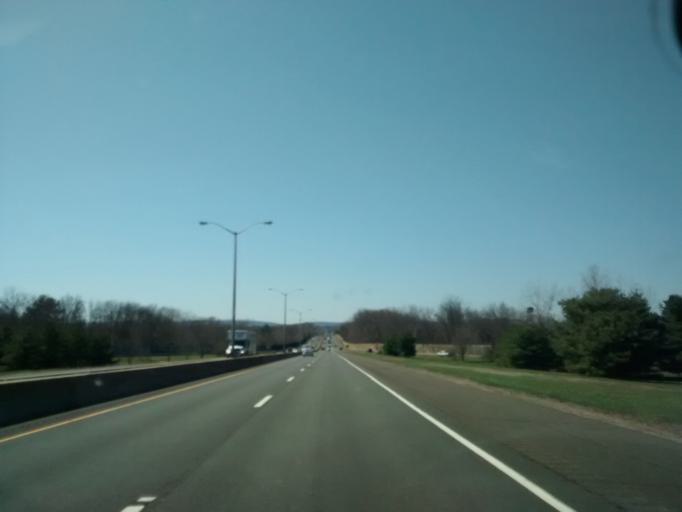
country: US
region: Connecticut
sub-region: Hartford County
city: South Windsor
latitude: 41.8058
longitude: -72.6157
